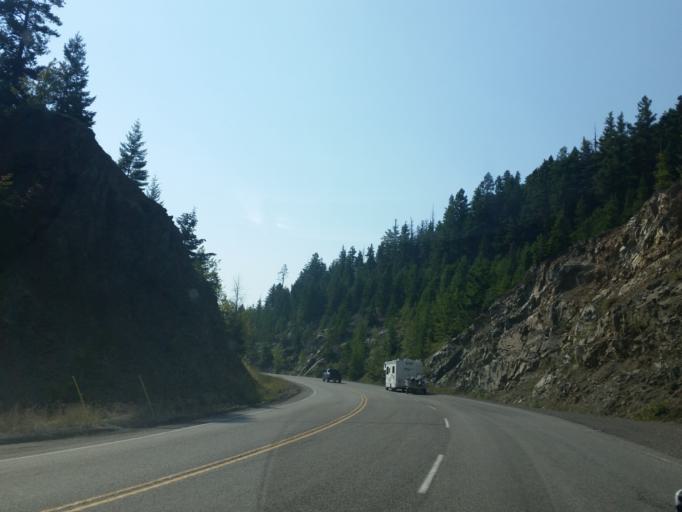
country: CA
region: British Columbia
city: Princeton
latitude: 49.3597
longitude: -120.5691
